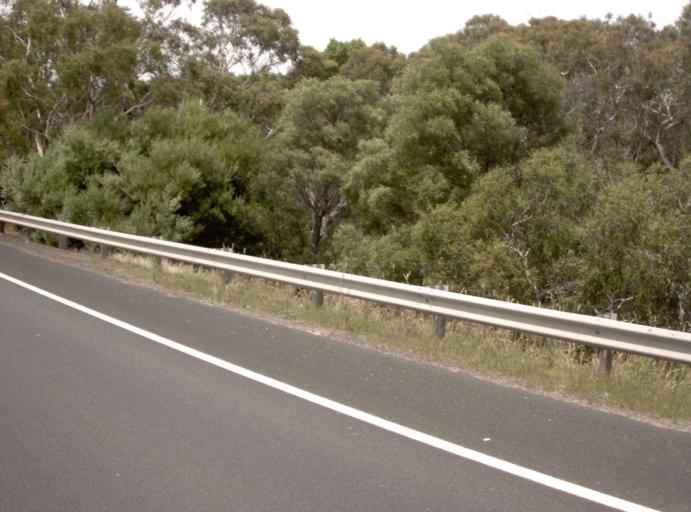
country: AU
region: Victoria
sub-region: Mornington Peninsula
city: Mount Martha
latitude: -38.2822
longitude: 145.0536
